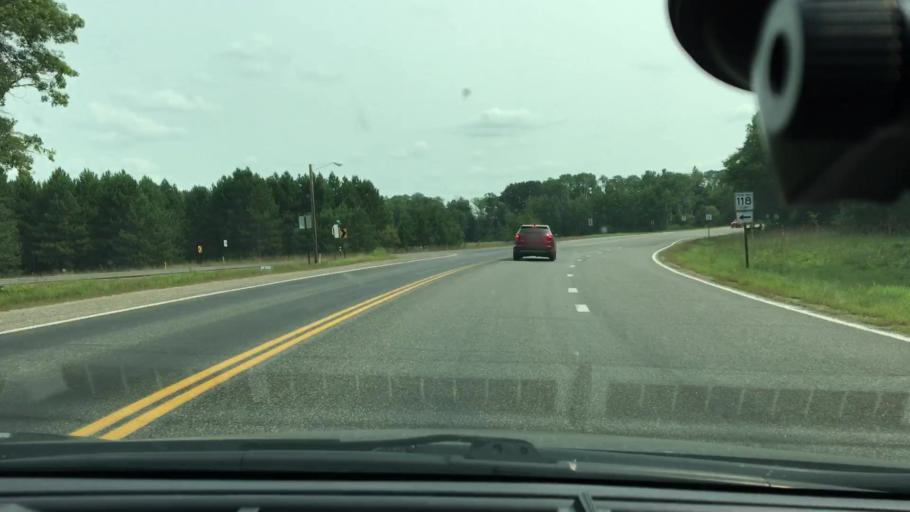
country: US
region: Minnesota
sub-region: Crow Wing County
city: Breezy Point
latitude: 46.5292
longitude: -94.1835
